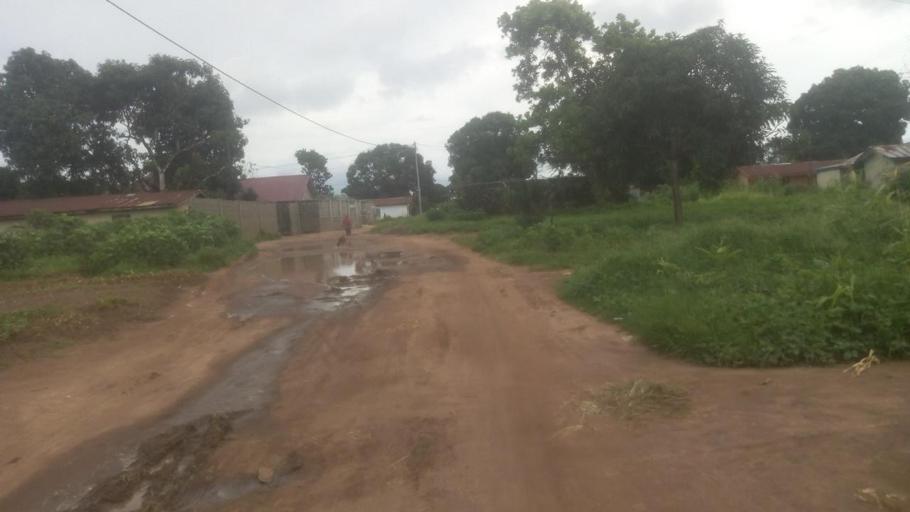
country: SL
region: Northern Province
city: Masoyila
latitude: 8.6036
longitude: -13.1853
